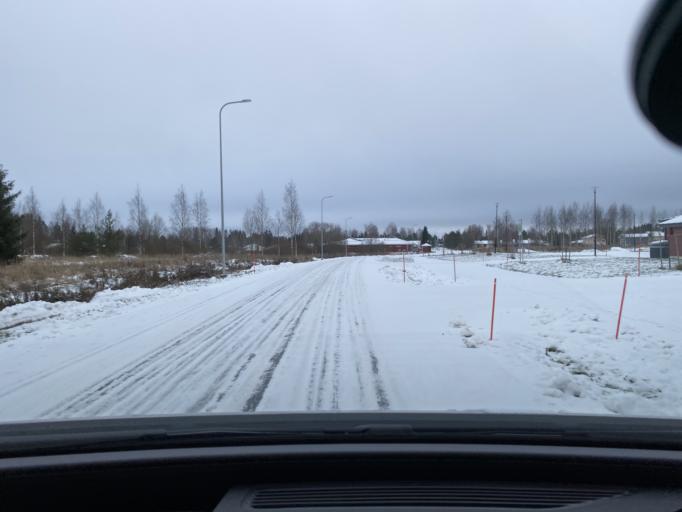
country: FI
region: Pirkanmaa
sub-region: Lounais-Pirkanmaa
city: Punkalaidun
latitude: 61.1194
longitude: 23.1145
